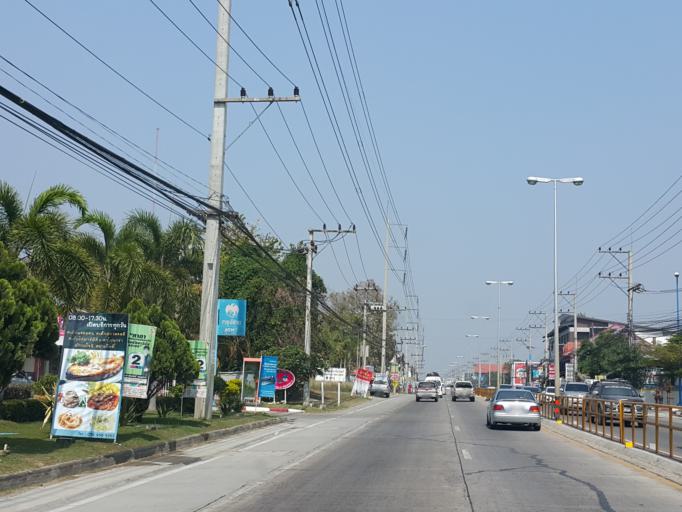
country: TH
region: Chiang Mai
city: San Sai
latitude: 18.9018
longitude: 98.9501
